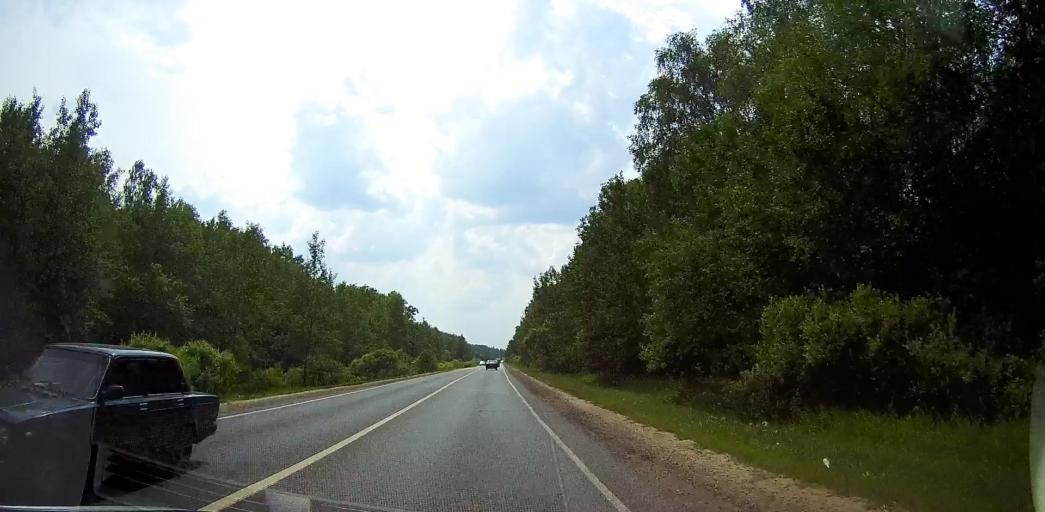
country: RU
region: Moskovskaya
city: Stupino
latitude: 54.9225
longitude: 38.1137
